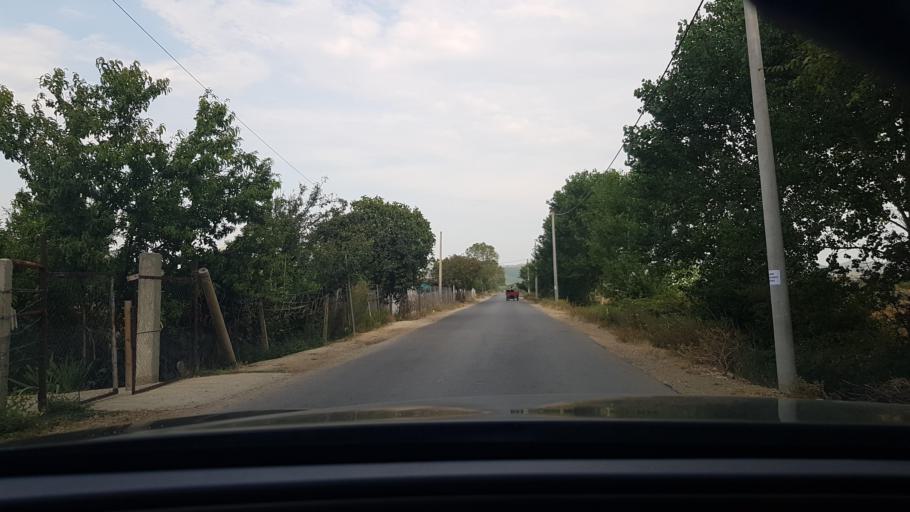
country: AL
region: Durres
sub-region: Rrethi i Durresit
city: Katundi i Ri
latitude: 41.4848
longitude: 19.5272
